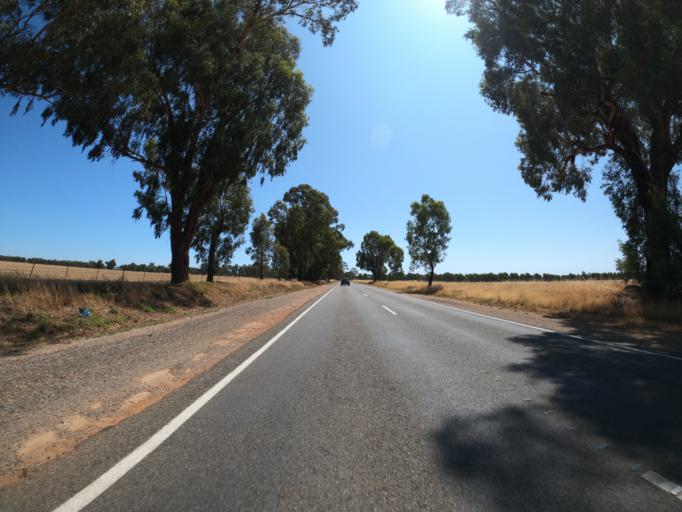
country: AU
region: Victoria
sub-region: Moira
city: Yarrawonga
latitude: -36.0227
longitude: 146.1308
